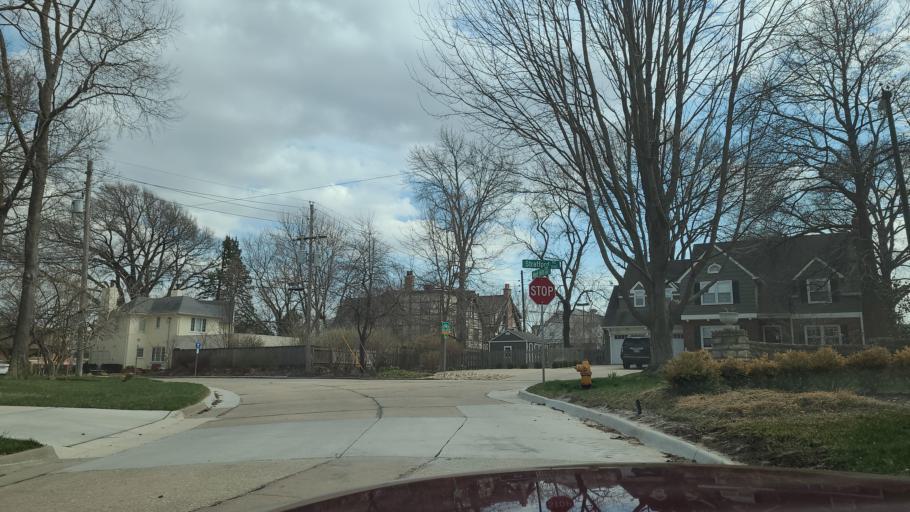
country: US
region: Kansas
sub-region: Douglas County
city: Lawrence
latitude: 38.9618
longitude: -95.2522
